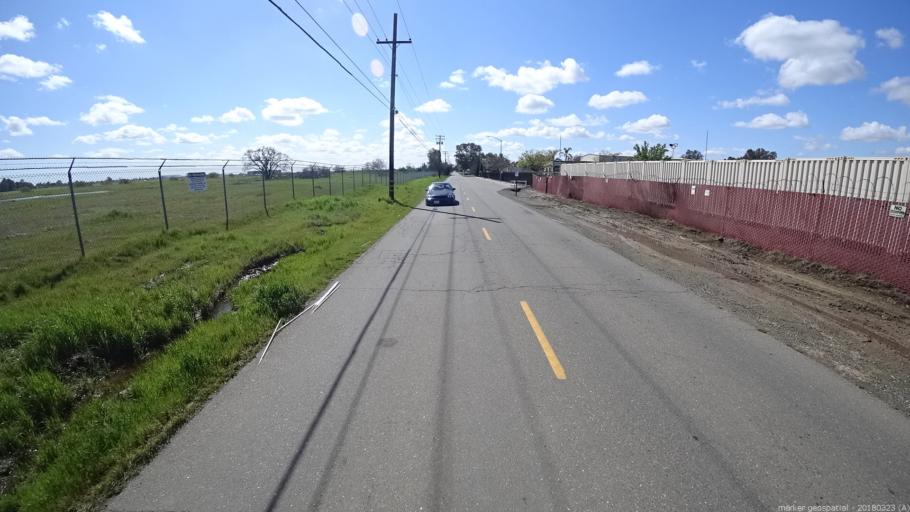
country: US
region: California
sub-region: Sacramento County
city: North Highlands
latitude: 38.6883
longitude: -121.4060
